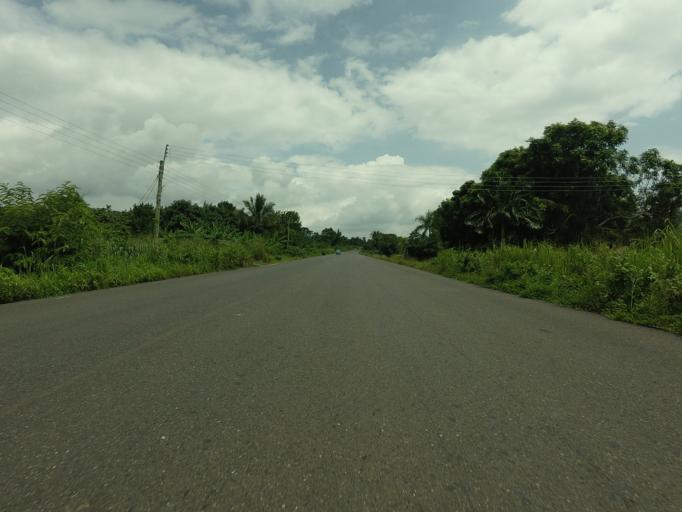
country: GH
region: Volta
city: Ho
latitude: 6.5461
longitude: 0.2516
